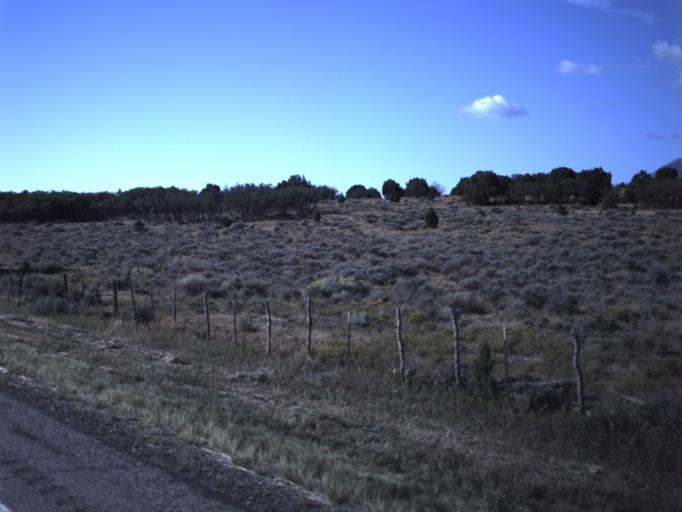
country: US
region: Utah
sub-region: San Juan County
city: Monticello
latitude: 37.8962
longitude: -109.3426
